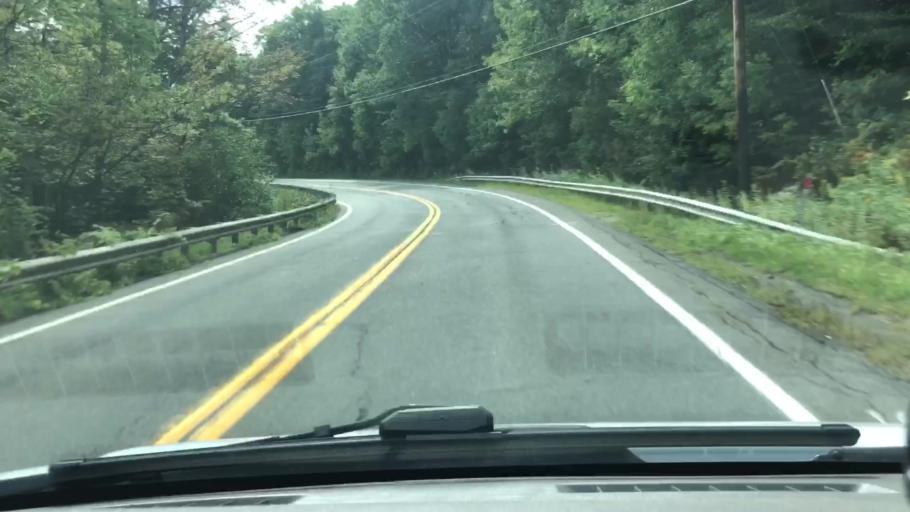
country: US
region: Massachusetts
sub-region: Berkshire County
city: North Adams
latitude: 42.6780
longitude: -73.0172
